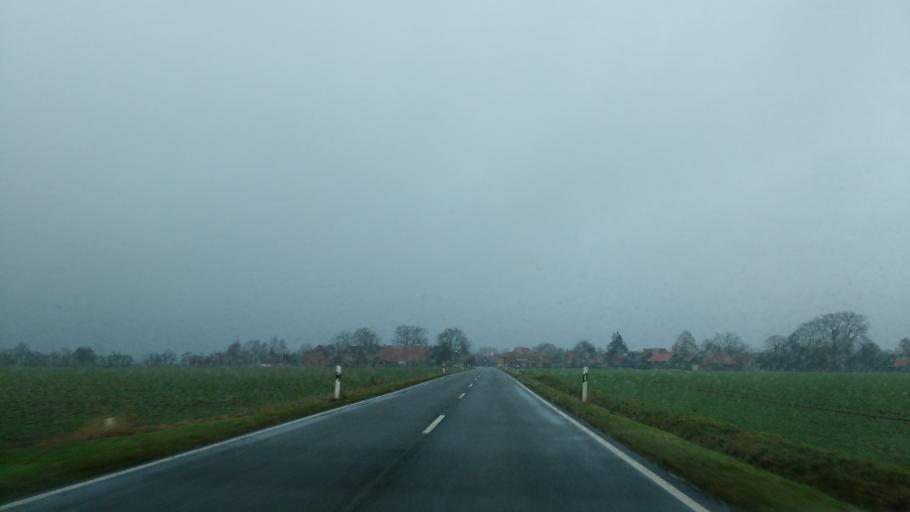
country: DE
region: Lower Saxony
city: Gilten
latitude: 52.6773
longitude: 9.5737
